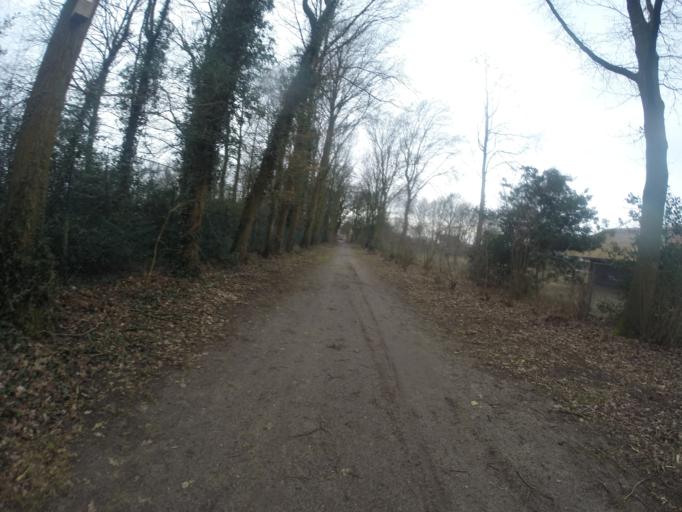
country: NL
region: Gelderland
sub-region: Gemeente Bronckhorst
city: Zelhem
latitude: 52.0083
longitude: 6.3594
